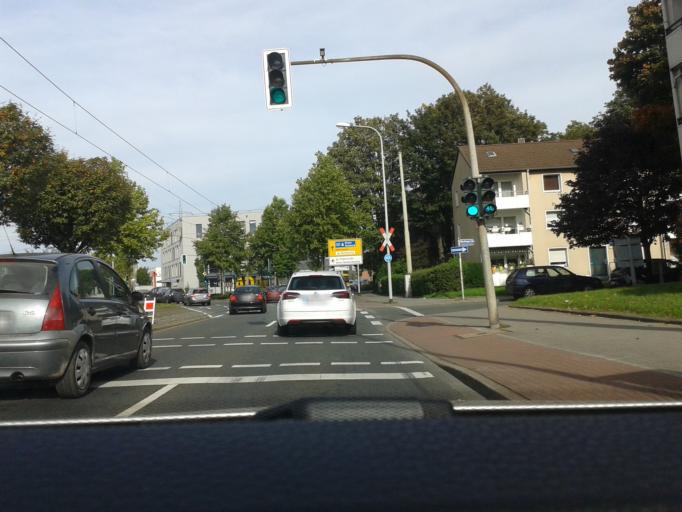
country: DE
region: North Rhine-Westphalia
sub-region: Regierungsbezirk Dusseldorf
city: Muelheim (Ruhr)
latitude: 51.4487
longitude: 6.8835
